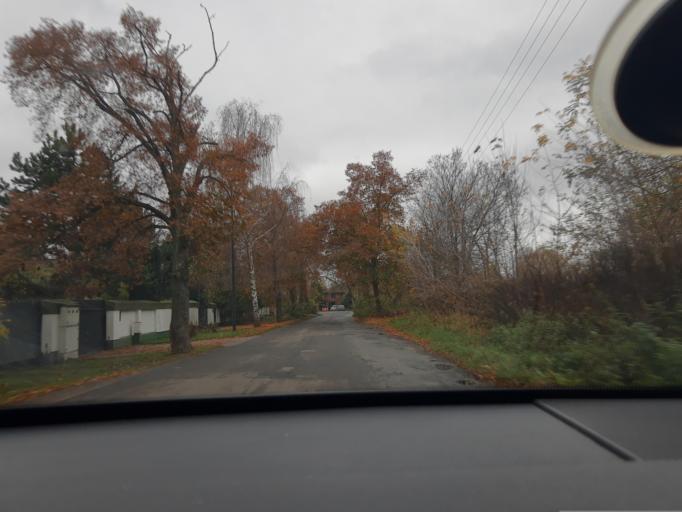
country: PL
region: Lodz Voivodeship
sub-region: Powiat pabianicki
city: Konstantynow Lodzki
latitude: 51.7445
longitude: 19.3714
